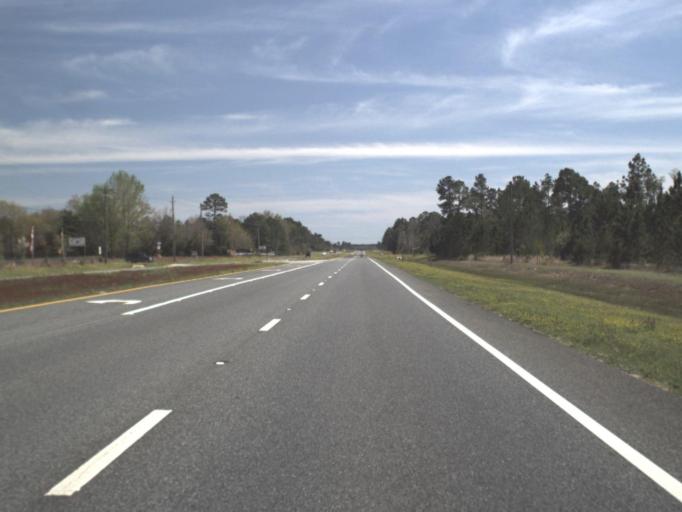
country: US
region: Florida
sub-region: Bay County
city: Lynn Haven
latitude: 30.3686
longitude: -85.6743
